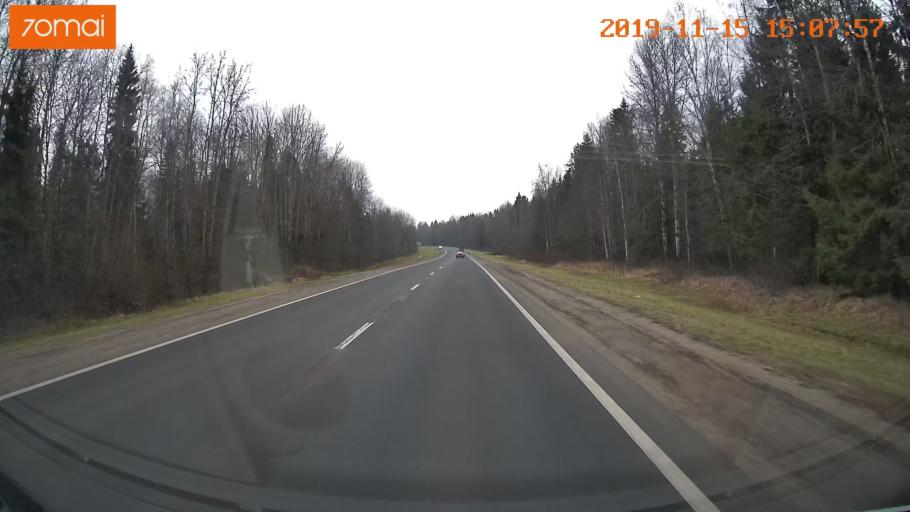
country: RU
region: Jaroslavl
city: Prechistoye
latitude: 58.3774
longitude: 40.2848
